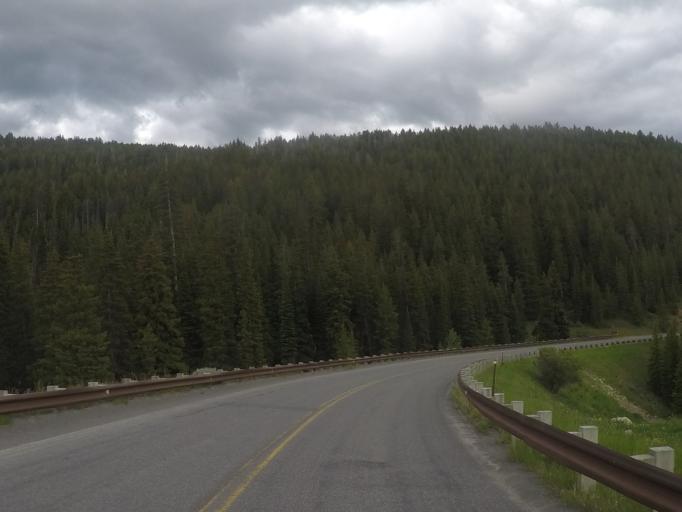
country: US
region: Wyoming
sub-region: Big Horn County
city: Greybull
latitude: 44.5859
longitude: -107.5329
